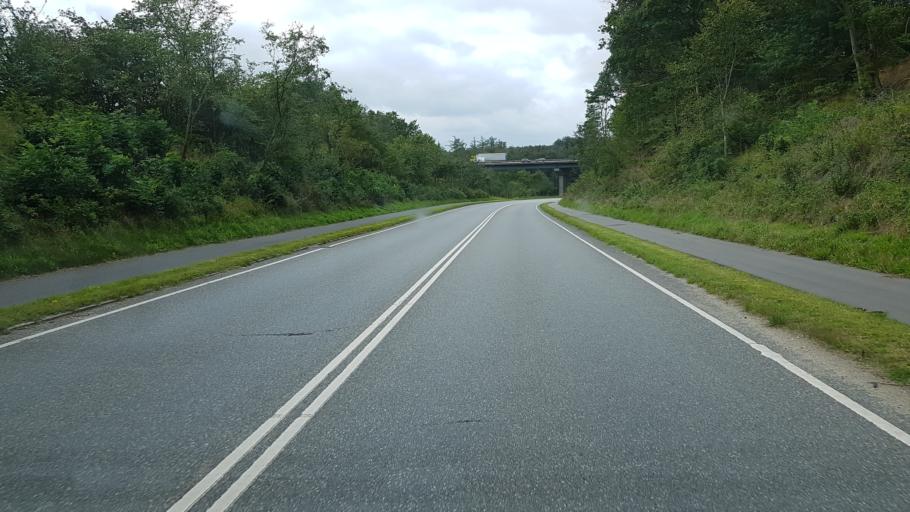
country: DK
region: South Denmark
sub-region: Kolding Kommune
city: Kolding
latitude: 55.4821
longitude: 9.4270
